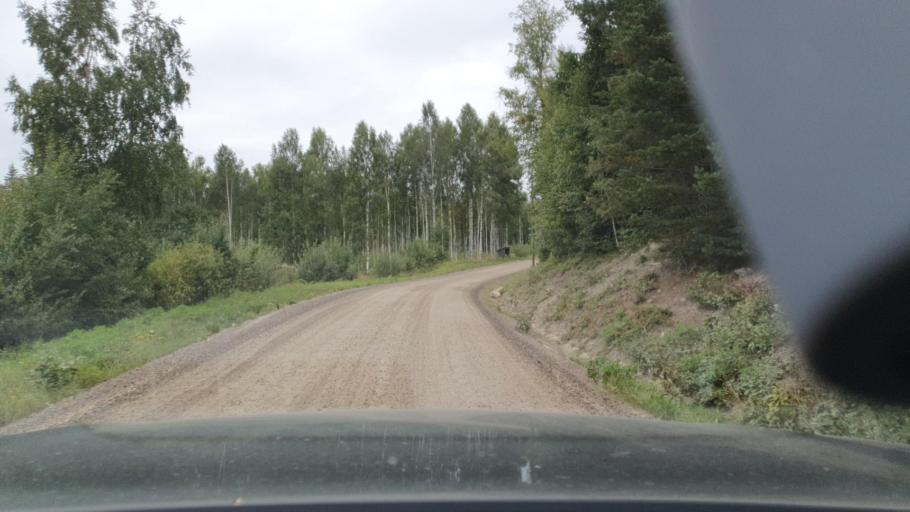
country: SE
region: Vaermland
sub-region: Arvika Kommun
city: Arvika
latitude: 59.9403
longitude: 12.6609
